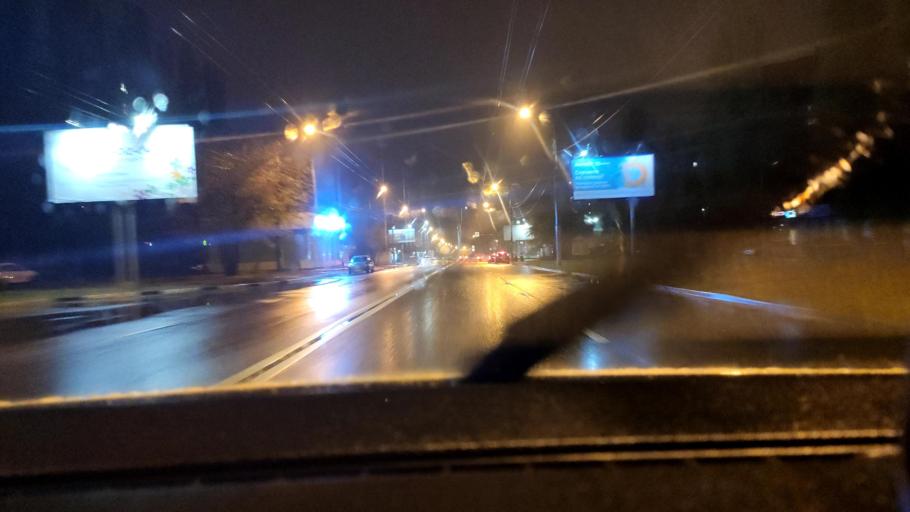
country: RU
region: Voronezj
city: Podgornoye
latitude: 51.7030
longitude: 39.1483
